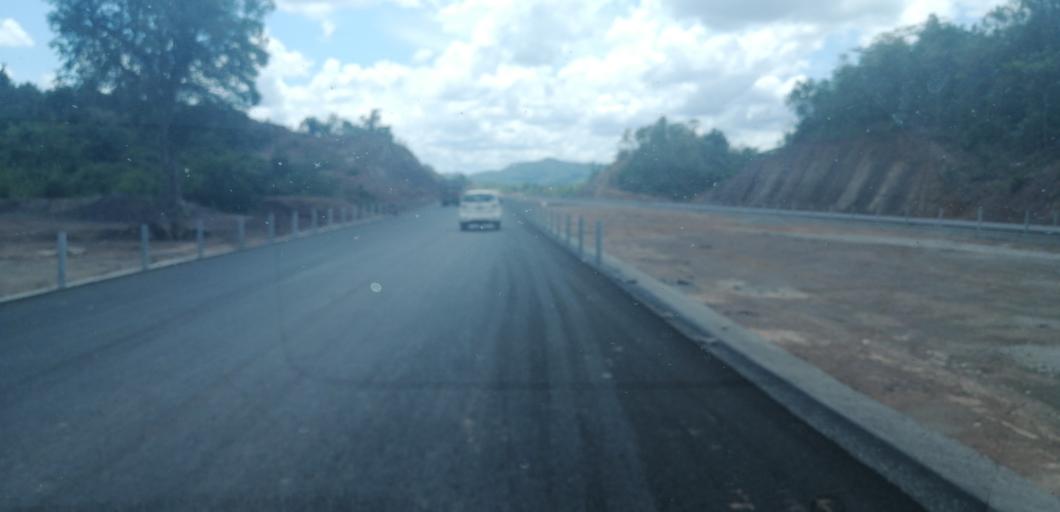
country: LA
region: Vientiane
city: Muang Phon-Hong
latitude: 18.5525
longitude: 102.3505
